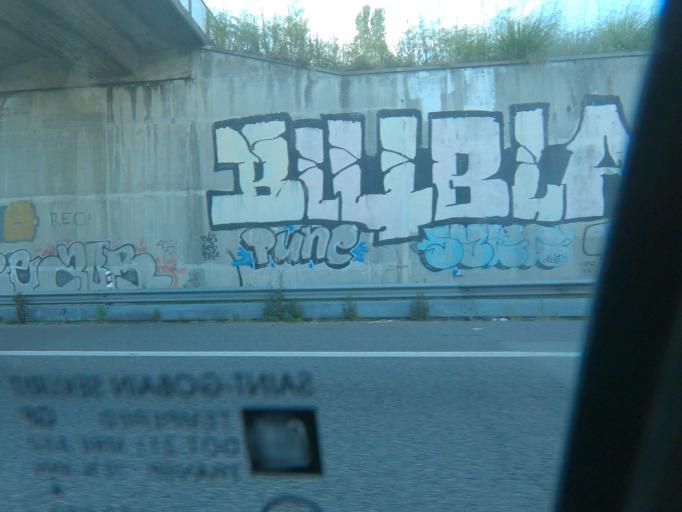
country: PT
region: Porto
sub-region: Matosinhos
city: Senhora da Hora
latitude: 41.1696
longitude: -8.6390
